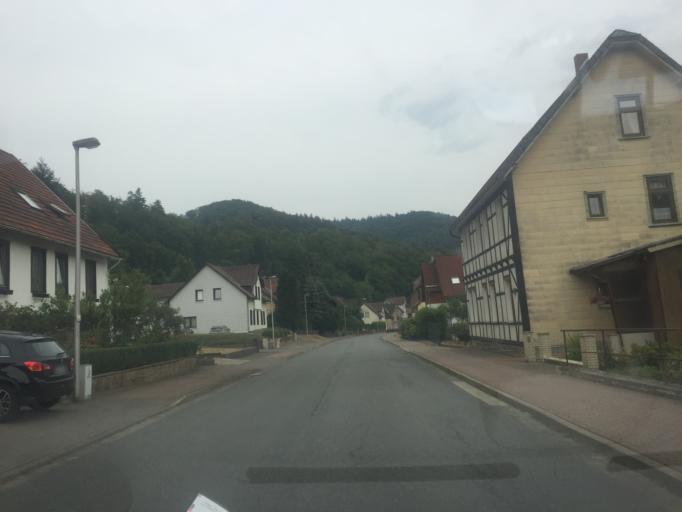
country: DE
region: Lower Saxony
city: Wieda
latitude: 51.6417
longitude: 10.5839
